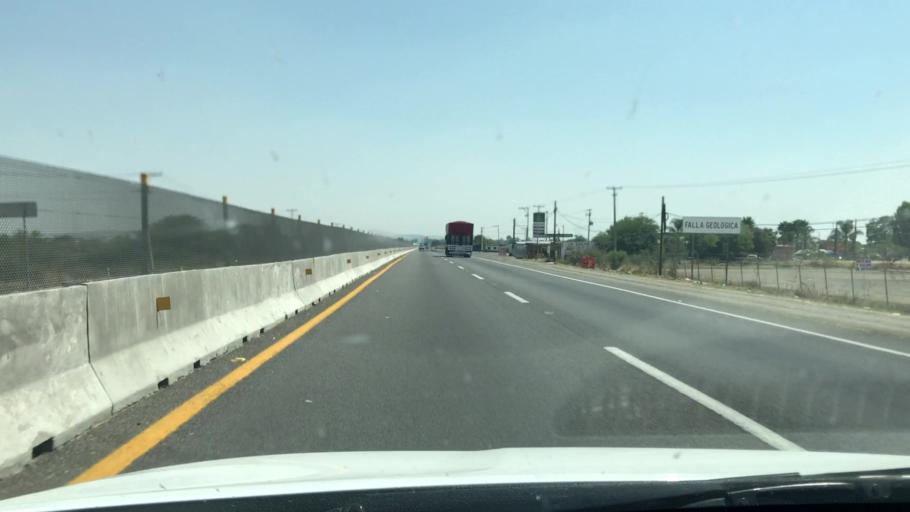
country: MX
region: Guanajuato
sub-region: Abasolo
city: San Bernardo Pena Blanca
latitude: 20.4734
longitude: -101.5019
